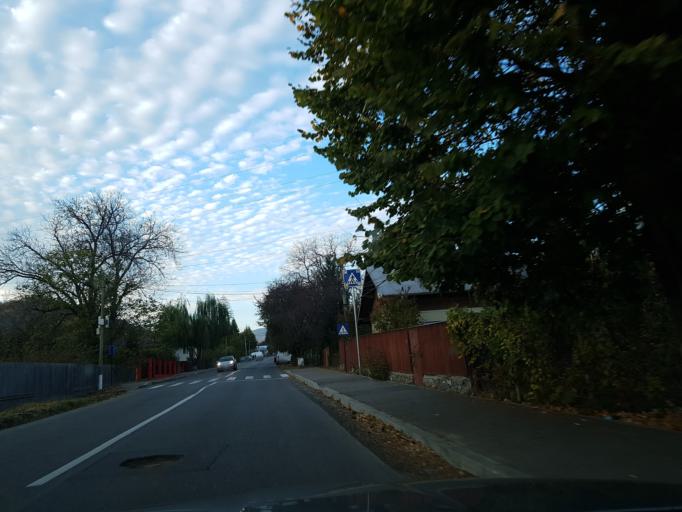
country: RO
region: Prahova
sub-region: Oras Breaza
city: Breaza de Sus
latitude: 45.1983
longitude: 25.6544
